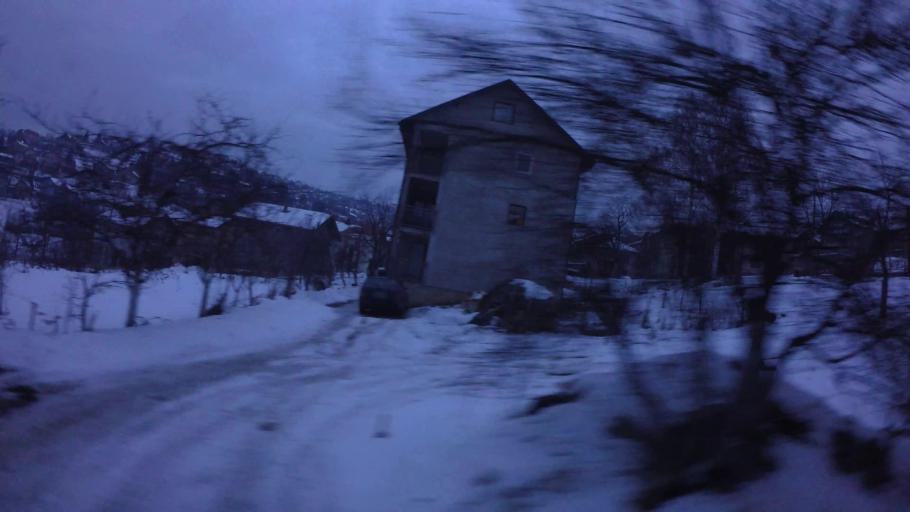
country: BA
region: Federation of Bosnia and Herzegovina
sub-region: Kanton Sarajevo
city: Sarajevo
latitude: 43.8540
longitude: 18.3410
